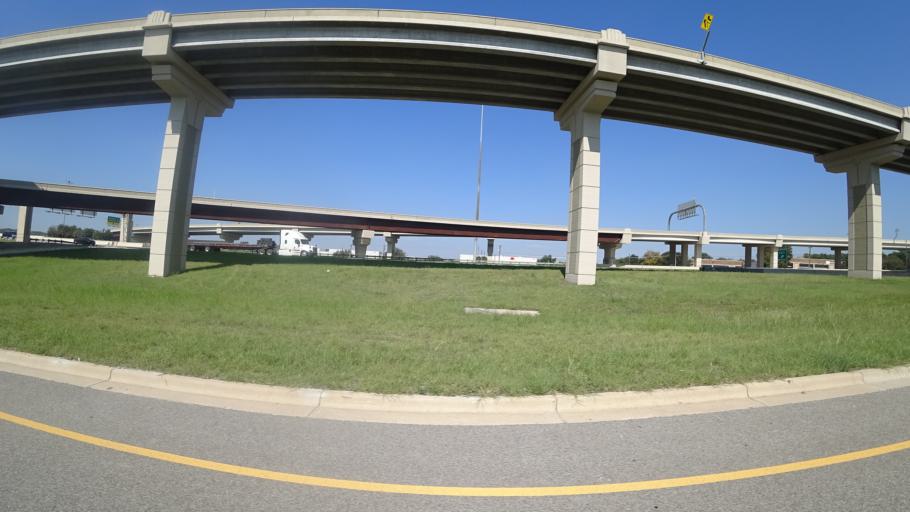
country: US
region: Texas
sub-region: Travis County
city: Austin
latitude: 30.3257
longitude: -97.6708
